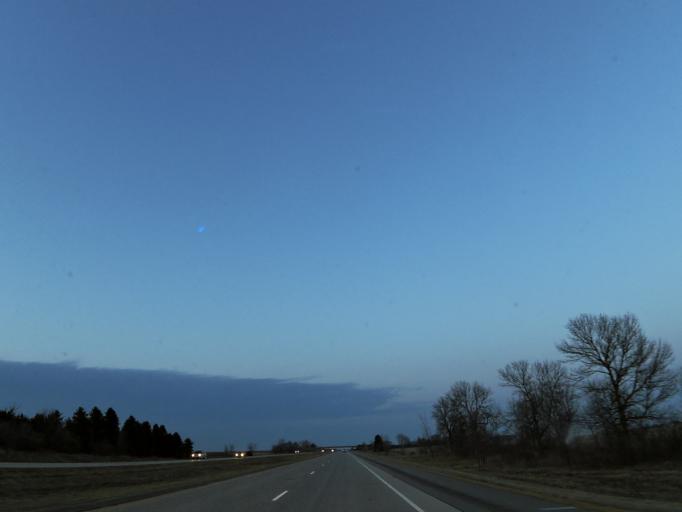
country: US
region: Minnesota
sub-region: Mower County
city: Grand Meadow
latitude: 43.7695
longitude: -92.6320
